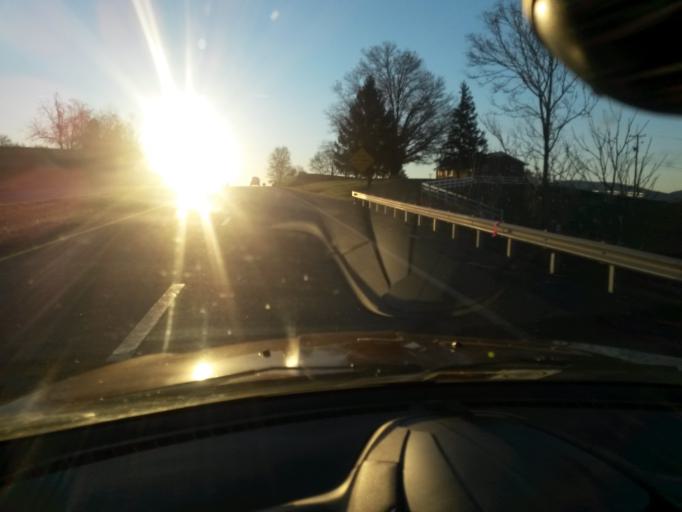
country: US
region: Virginia
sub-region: Franklin County
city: Rocky Mount
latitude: 37.0789
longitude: -79.9192
